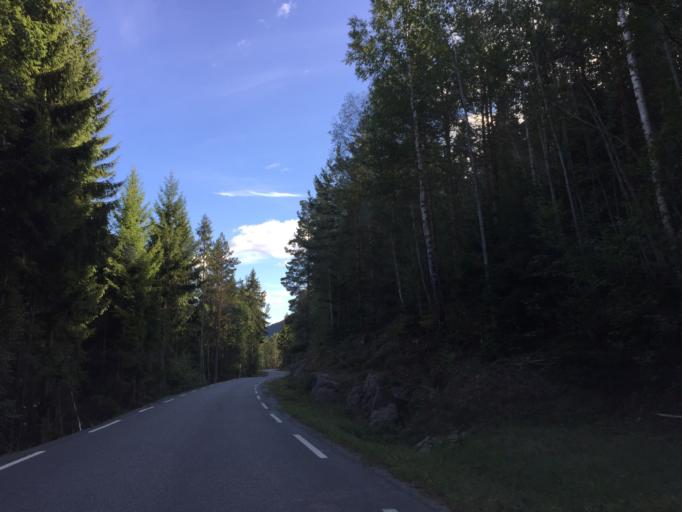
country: NO
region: Buskerud
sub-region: Ovre Eiker
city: Hokksund
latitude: 59.6498
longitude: 9.9182
